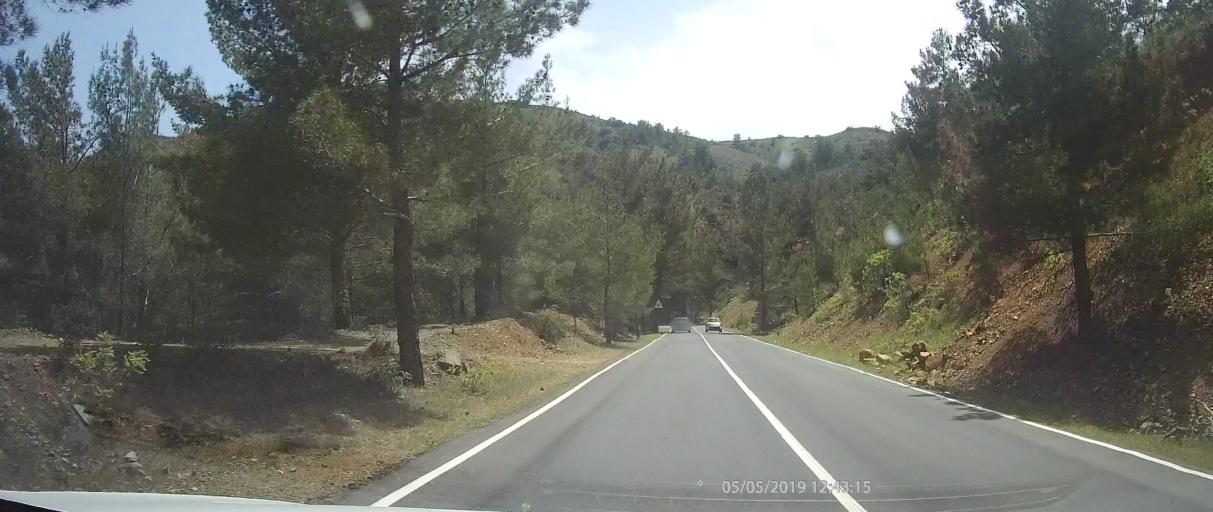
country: CY
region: Lefkosia
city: Kakopetria
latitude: 34.9695
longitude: 32.8136
